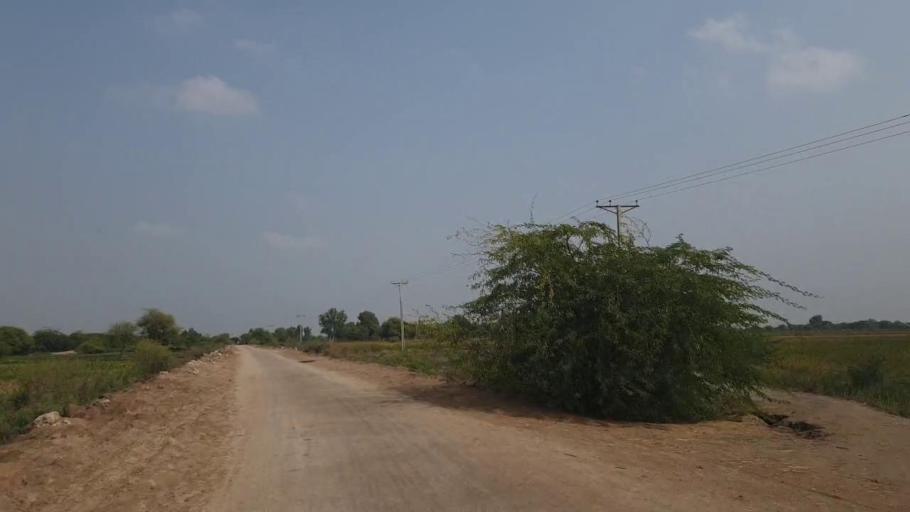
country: PK
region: Sindh
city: Badin
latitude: 24.5475
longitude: 68.7224
